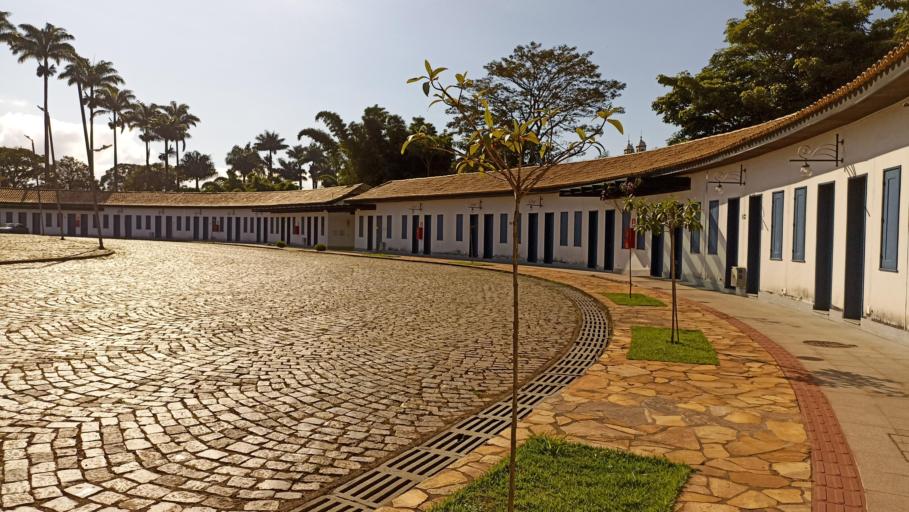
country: BR
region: Minas Gerais
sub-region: Congonhas
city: Congonhas
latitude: -20.5068
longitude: -43.8631
